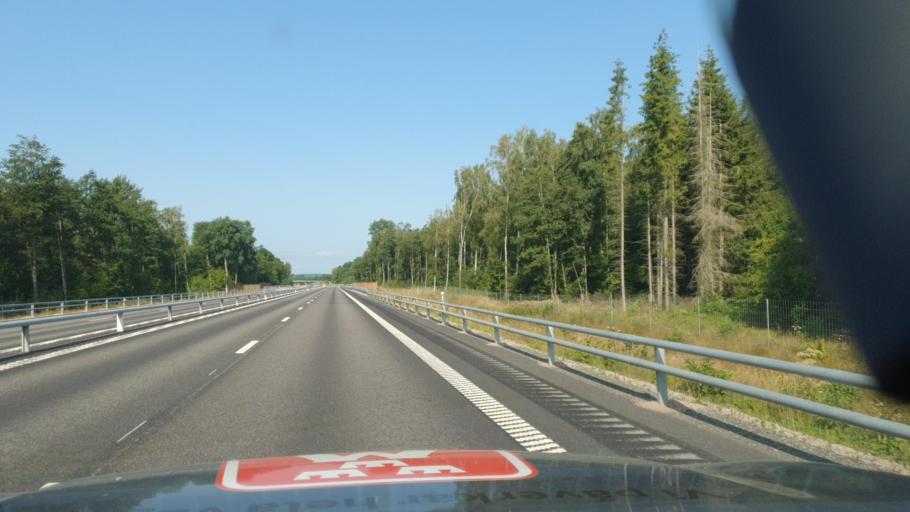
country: SE
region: Skane
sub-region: Kristianstads Kommun
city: Onnestad
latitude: 55.9611
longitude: 13.9718
